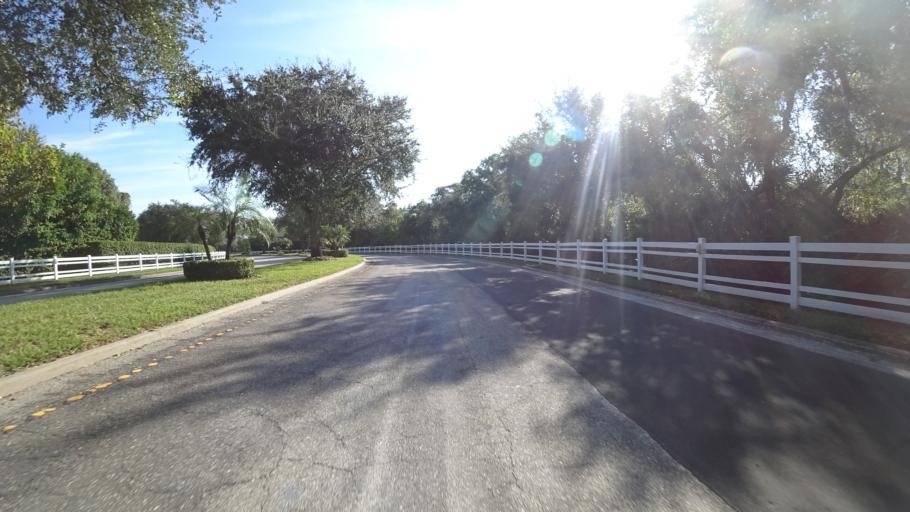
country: US
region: Florida
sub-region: Sarasota County
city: Desoto Lakes
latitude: 27.4177
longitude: -82.4817
